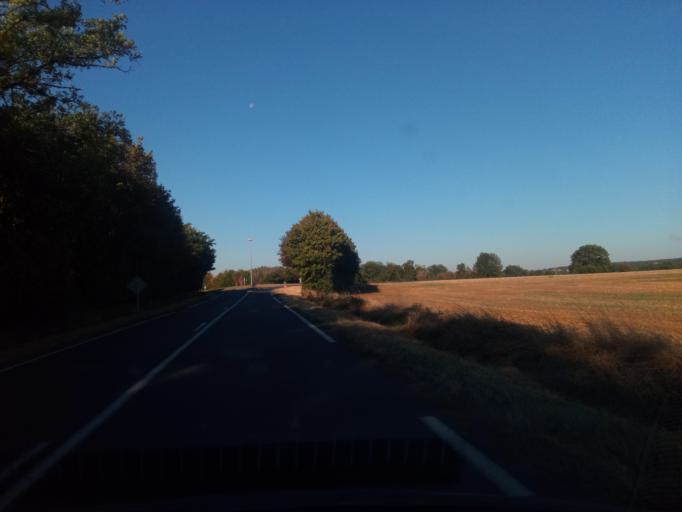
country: FR
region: Poitou-Charentes
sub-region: Departement de la Vienne
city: Lussac-les-Chateaux
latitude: 46.4006
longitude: 0.7433
